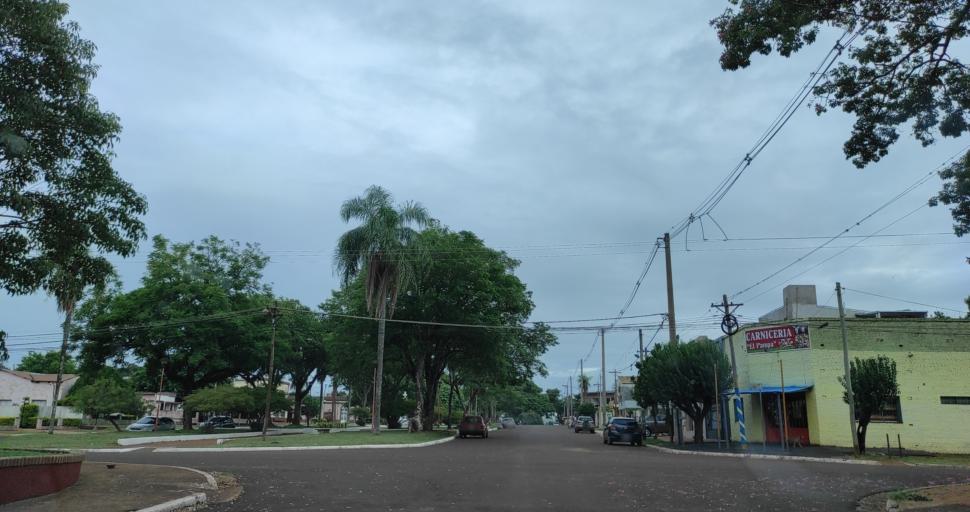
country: AR
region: Misiones
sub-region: Departamento de Apostoles
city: San Jose
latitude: -27.7694
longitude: -55.7794
